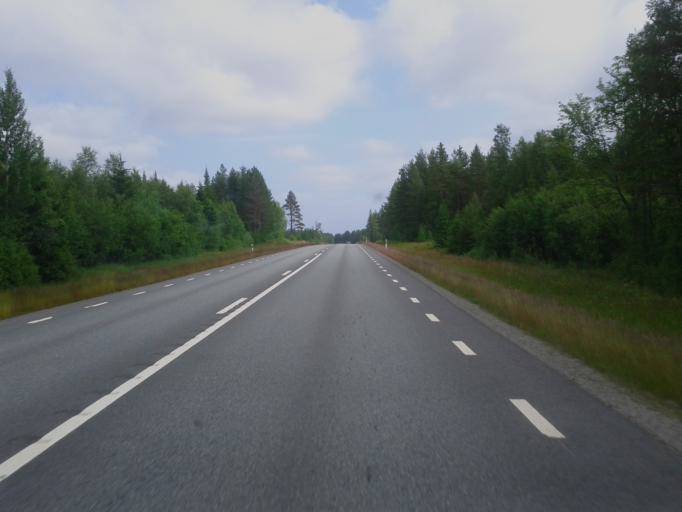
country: SE
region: Vaesterbotten
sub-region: Skelleftea Kommun
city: Burea
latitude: 64.3424
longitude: 21.2813
